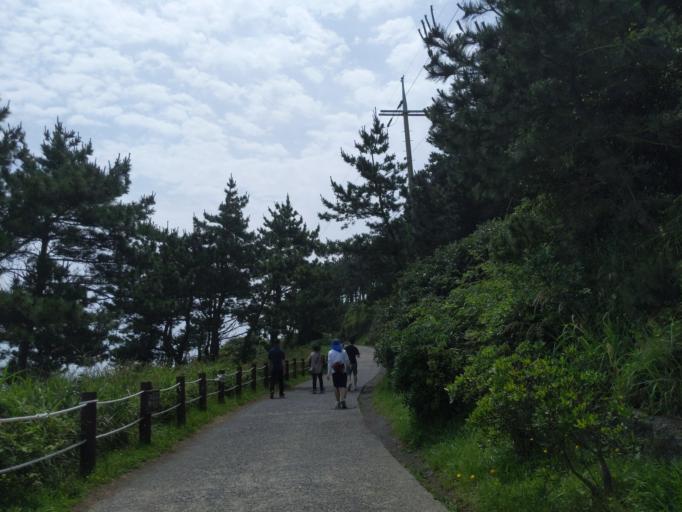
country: KR
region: Jeju-do
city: Gaigeturi
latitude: 33.2031
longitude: 126.2911
